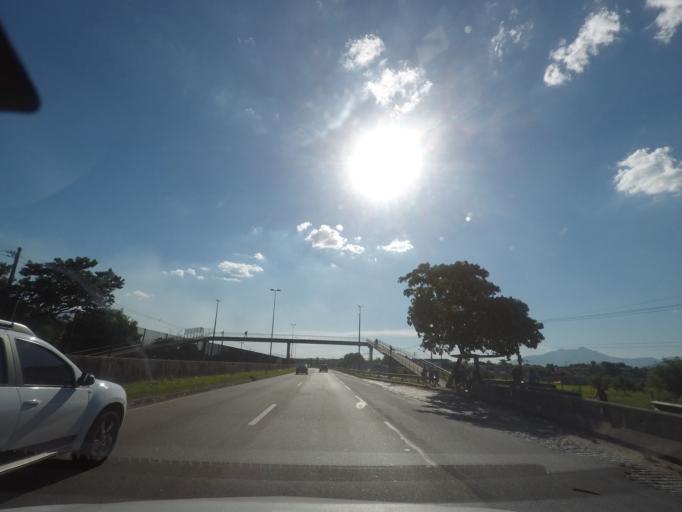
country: BR
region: Rio de Janeiro
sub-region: Duque De Caxias
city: Duque de Caxias
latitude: -22.6511
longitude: -43.2367
